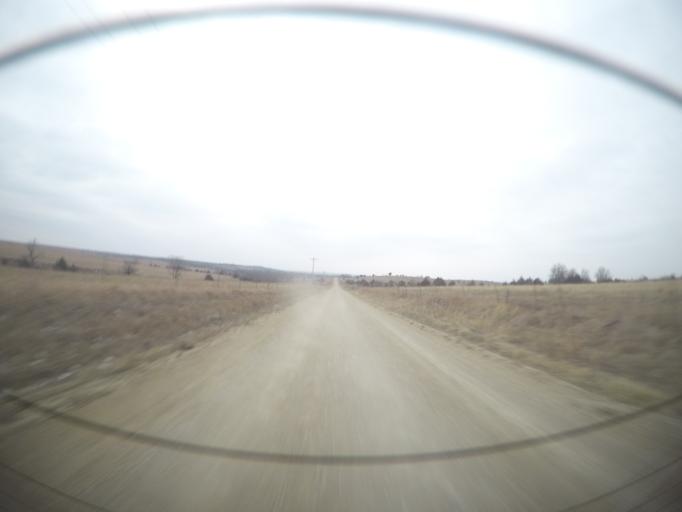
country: US
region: Kansas
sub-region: Pottawatomie County
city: Wamego
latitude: 39.1518
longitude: -96.2674
